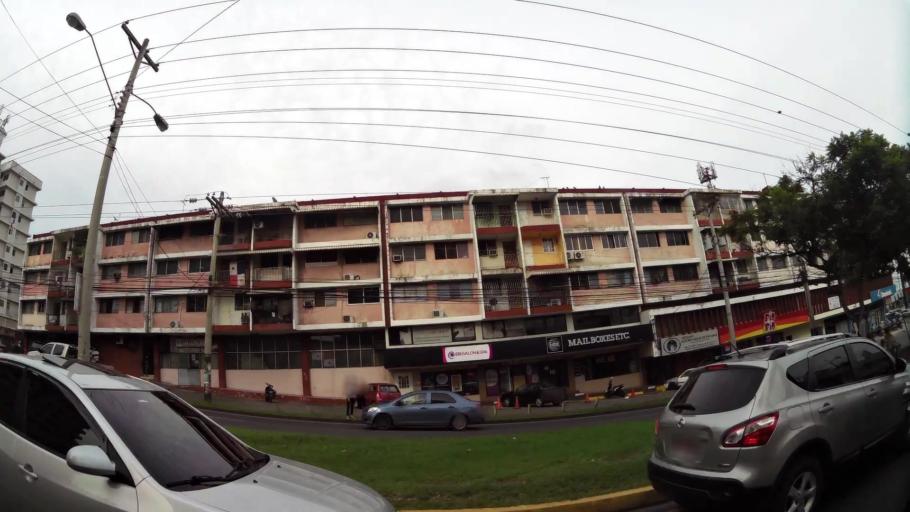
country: PA
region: Panama
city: Panama
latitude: 9.0090
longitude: -79.5079
